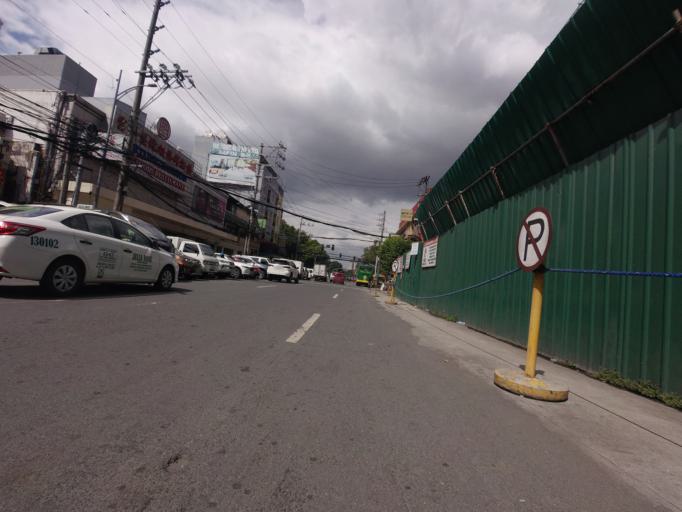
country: PH
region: Metro Manila
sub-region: City of Manila
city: Port Area
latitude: 14.5813
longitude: 120.9816
